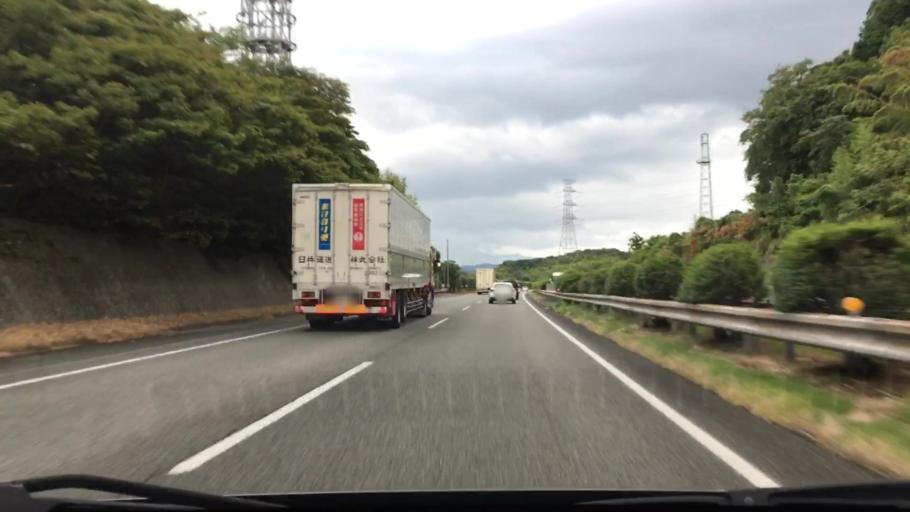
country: JP
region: Fukuoka
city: Miyata
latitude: 33.7500
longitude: 130.5865
